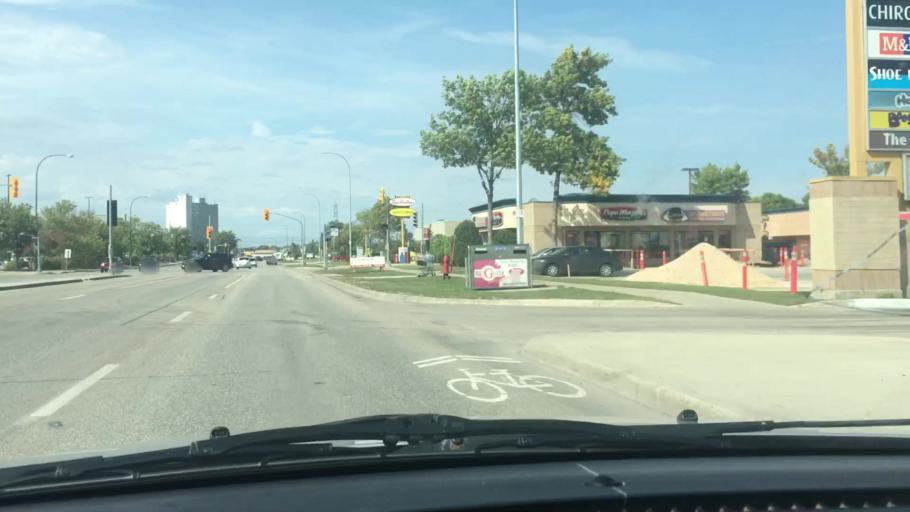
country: CA
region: Manitoba
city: Winnipeg
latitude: 49.8296
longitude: -97.1061
